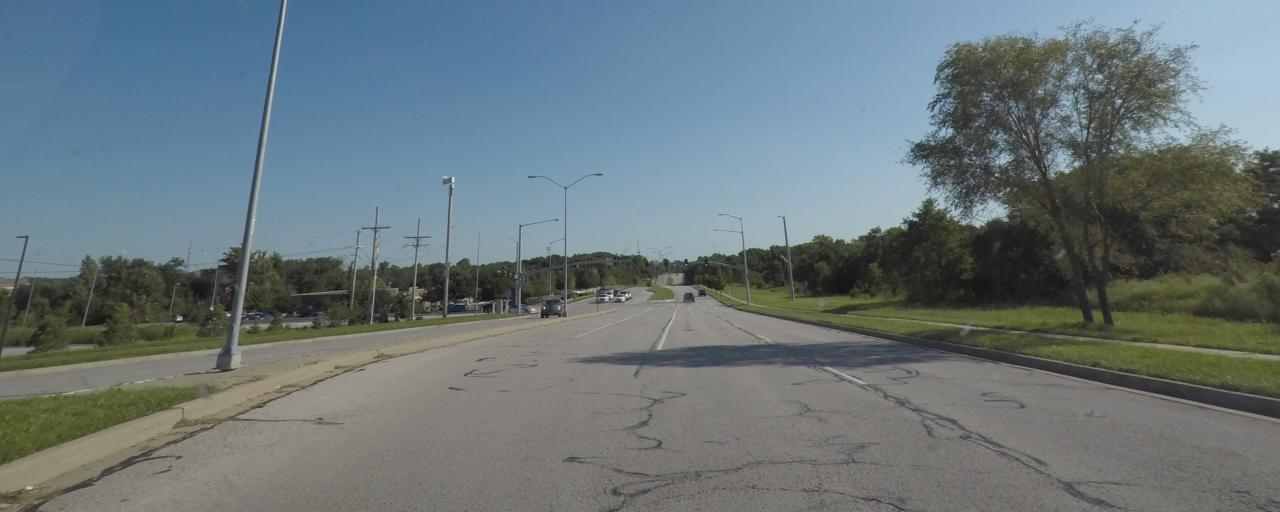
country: US
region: Missouri
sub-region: Clay County
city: Gladstone
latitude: 39.2540
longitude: -94.6009
